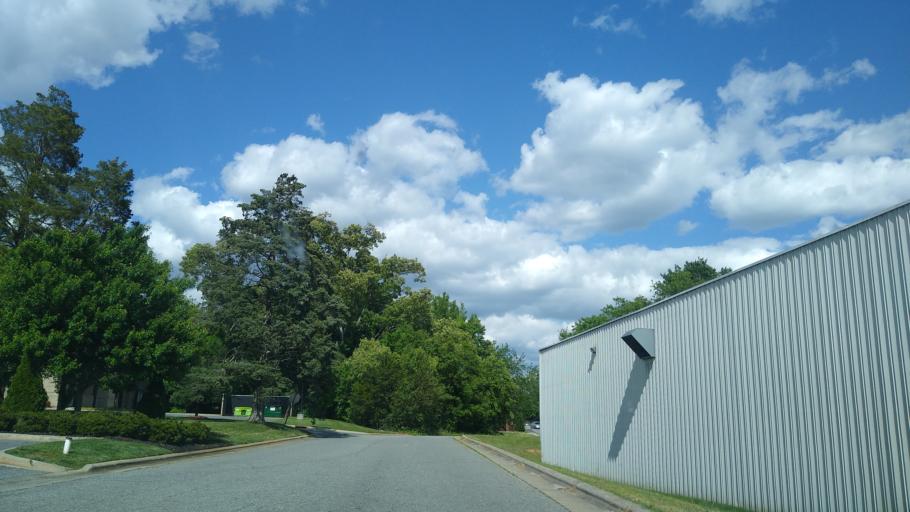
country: US
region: North Carolina
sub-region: Forsyth County
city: Kernersville
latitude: 36.1072
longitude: -80.0973
